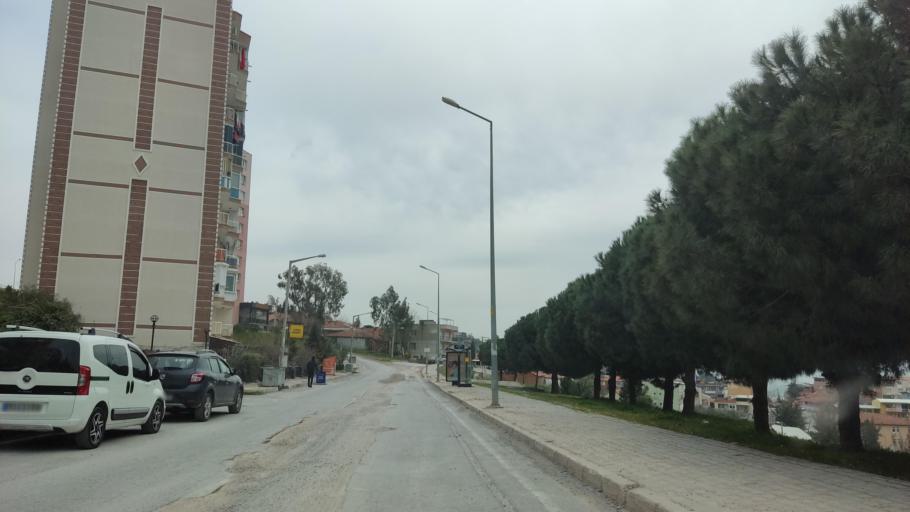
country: TR
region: Izmir
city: Karsiyaka
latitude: 38.5047
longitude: 27.0778
